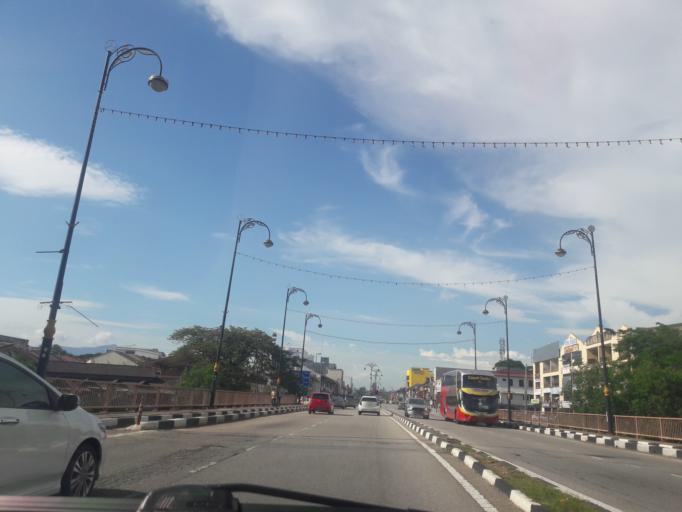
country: MY
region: Kedah
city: Sungai Petani
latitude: 5.6386
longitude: 100.4886
